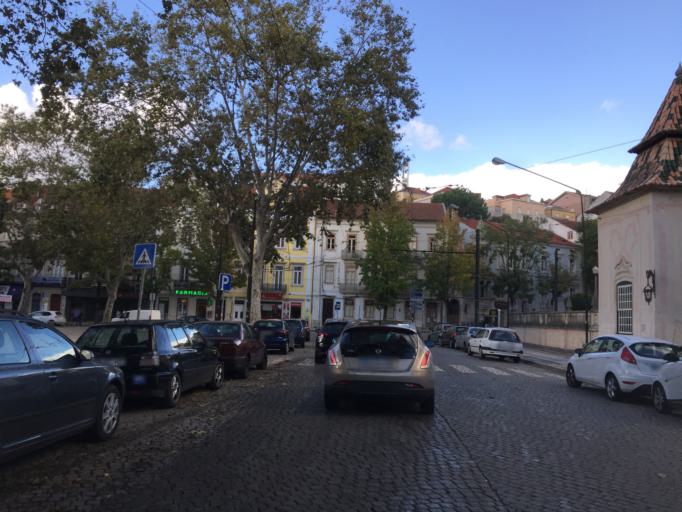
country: PT
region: Coimbra
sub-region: Coimbra
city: Coimbra
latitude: 40.2093
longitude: -8.4192
